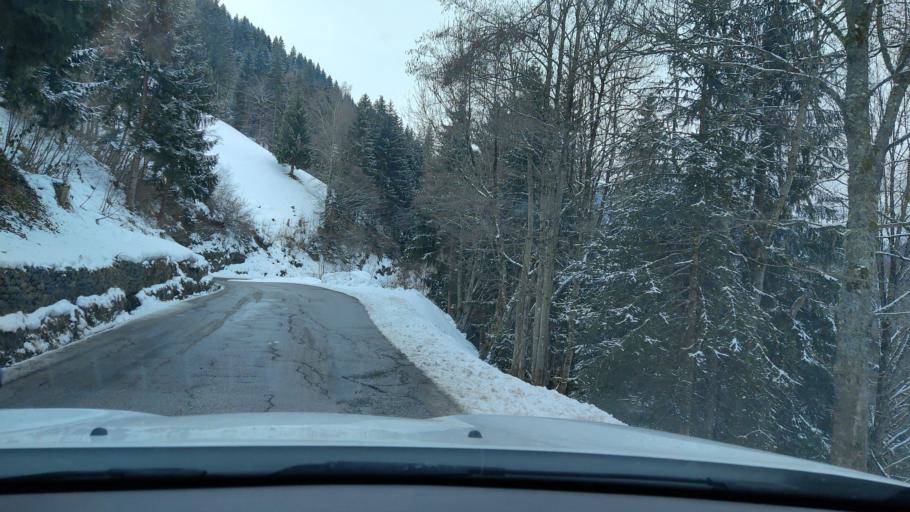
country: FR
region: Rhone-Alpes
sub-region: Departement de la Savoie
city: Beaufort
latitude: 45.7412
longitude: 6.5830
